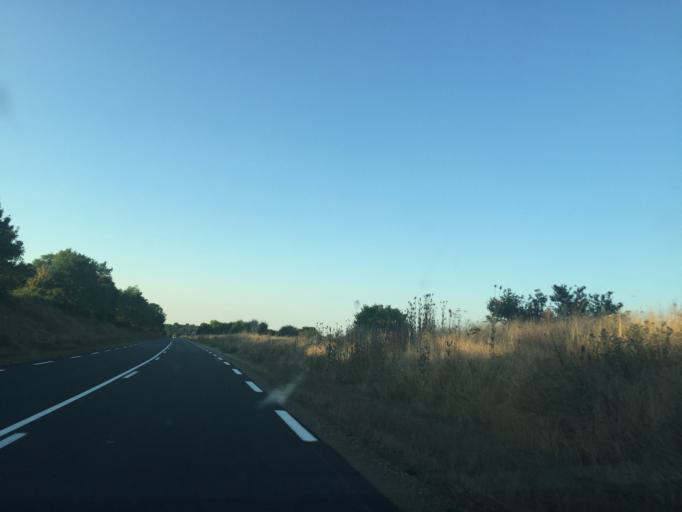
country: FR
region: Poitou-Charentes
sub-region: Departement de la Vienne
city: Lusignan
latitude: 46.4359
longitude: 0.1377
